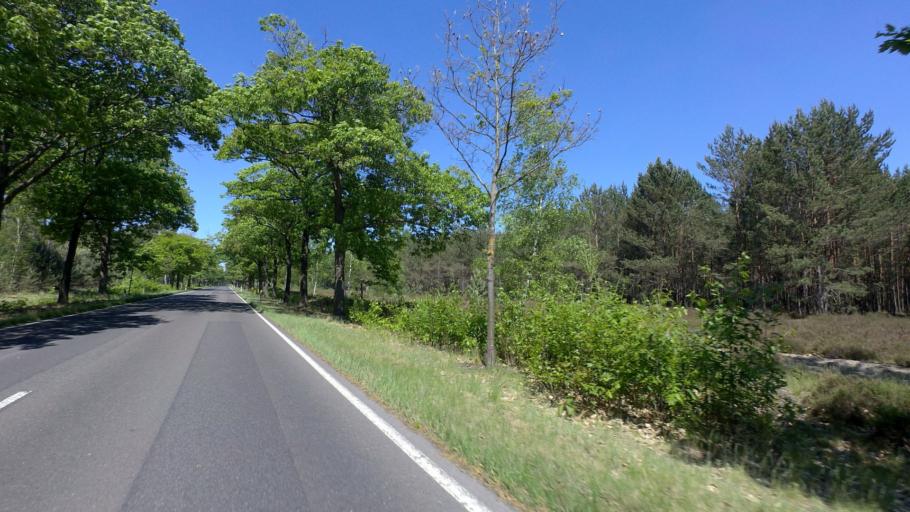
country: DE
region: Brandenburg
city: Drachhausen
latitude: 51.9094
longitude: 14.3530
